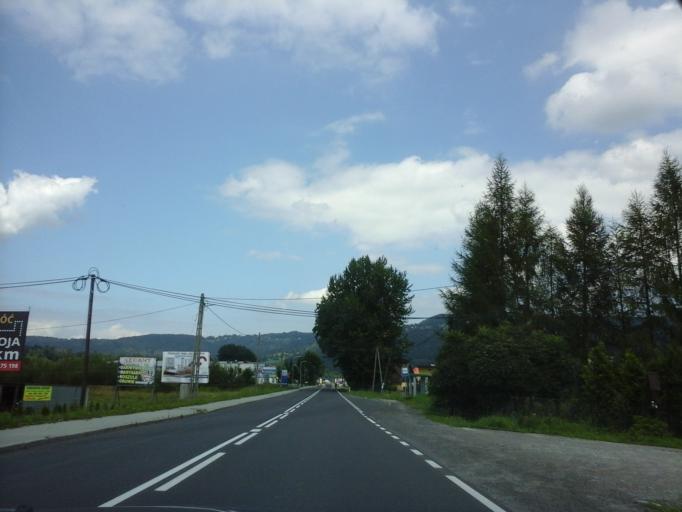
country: PL
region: Lesser Poland Voivodeship
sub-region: Powiat suski
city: Juszczyn
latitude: 49.7124
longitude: 19.6886
